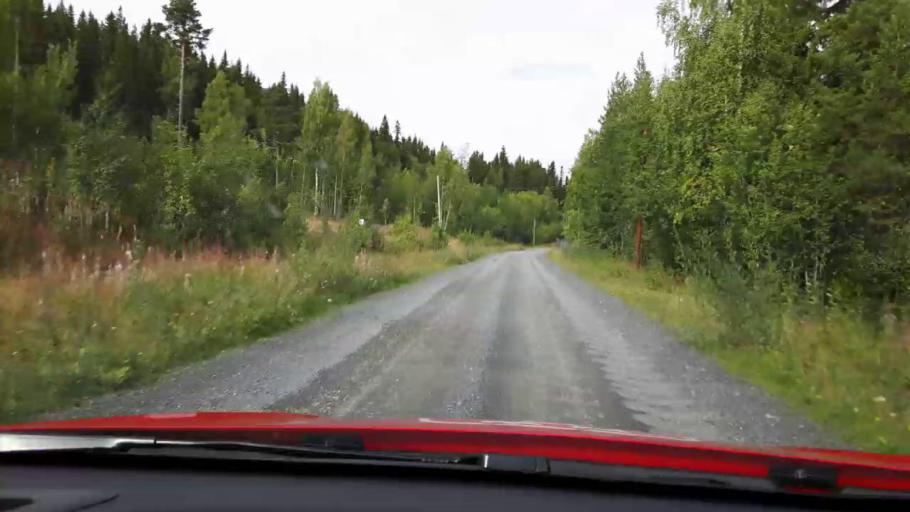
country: SE
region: Jaemtland
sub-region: Are Kommun
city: Jarpen
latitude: 63.2759
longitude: 13.7377
